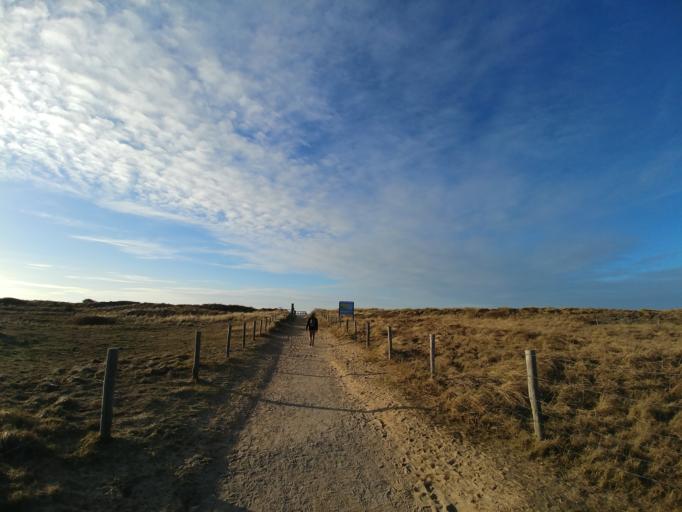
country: NL
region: South Holland
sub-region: Gemeente Den Haag
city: Scheveningen
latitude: 52.1255
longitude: 4.3022
